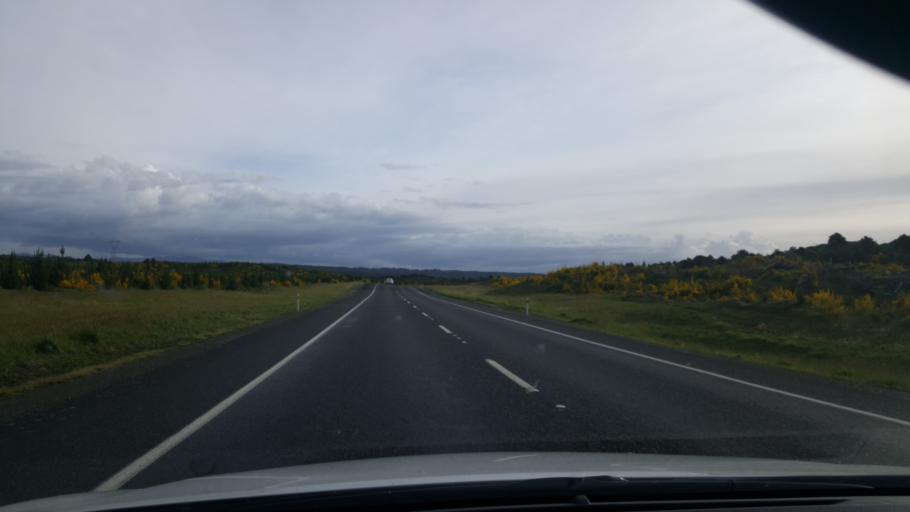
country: NZ
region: Waikato
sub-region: Taupo District
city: Taupo
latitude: -38.8481
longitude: 176.0567
